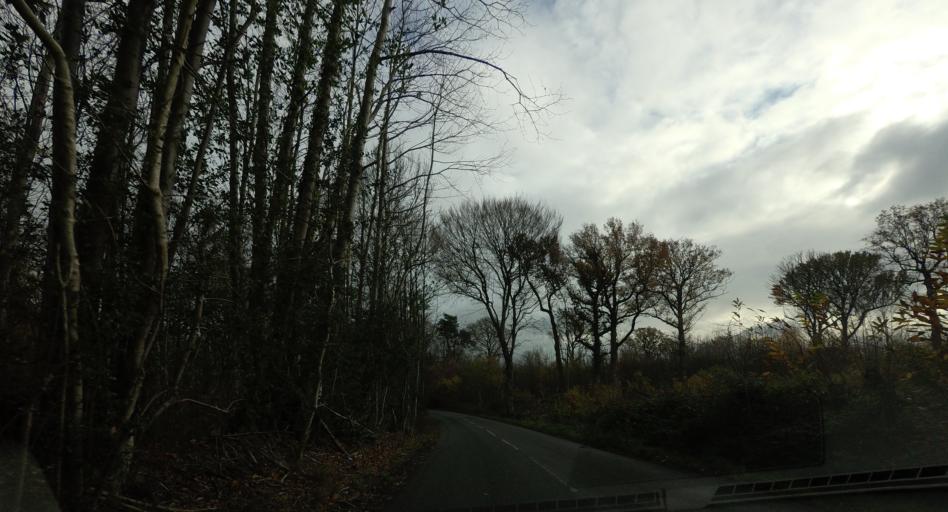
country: GB
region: England
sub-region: Kent
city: Paddock Wood
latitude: 51.1378
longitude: 0.4148
